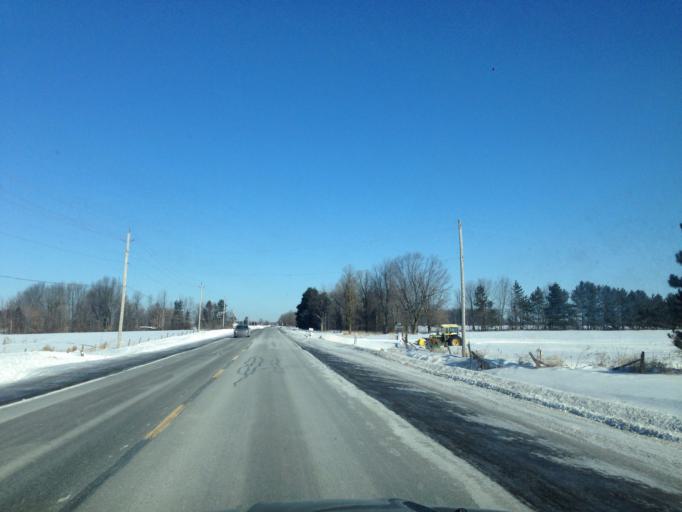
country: CA
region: Ontario
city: Clarence-Rockland
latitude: 45.2946
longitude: -75.4173
